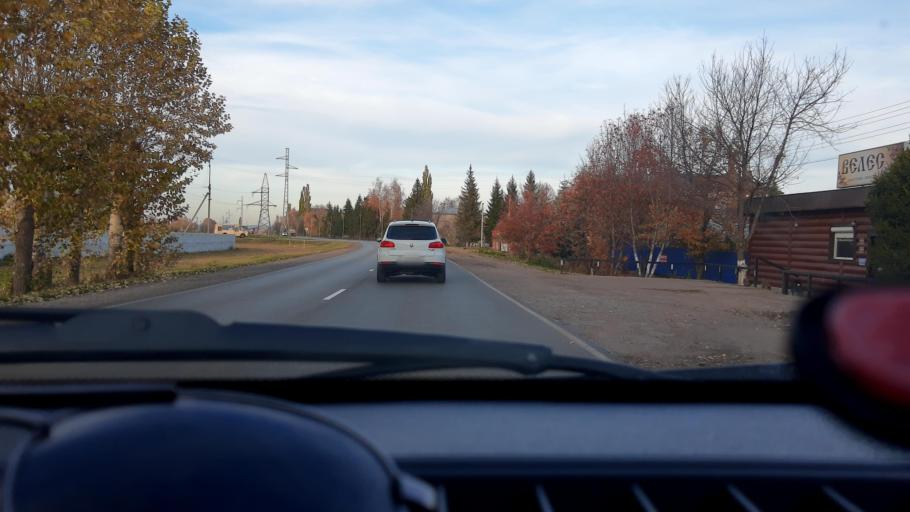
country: RU
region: Bashkortostan
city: Ufa
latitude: 54.8269
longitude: 55.9924
